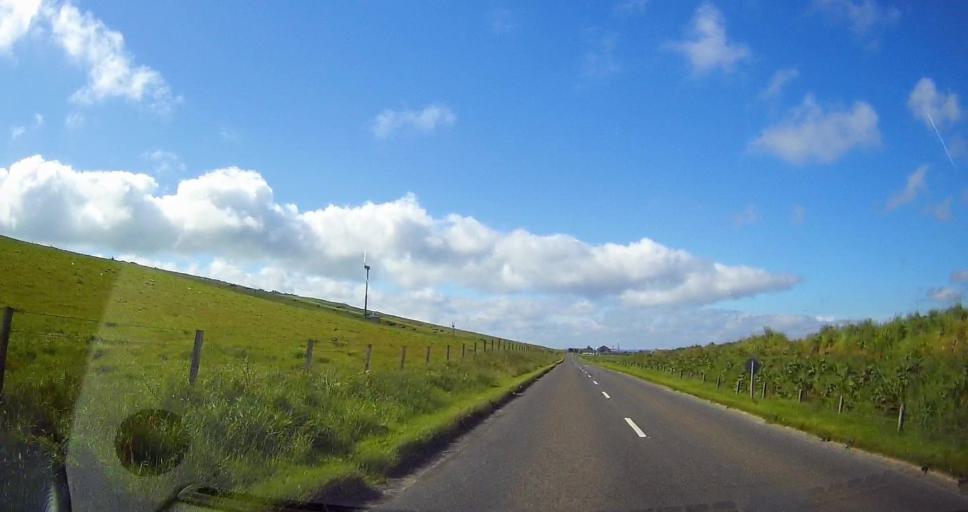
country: GB
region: Scotland
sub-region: Orkney Islands
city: Orkney
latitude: 58.9693
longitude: -2.9628
